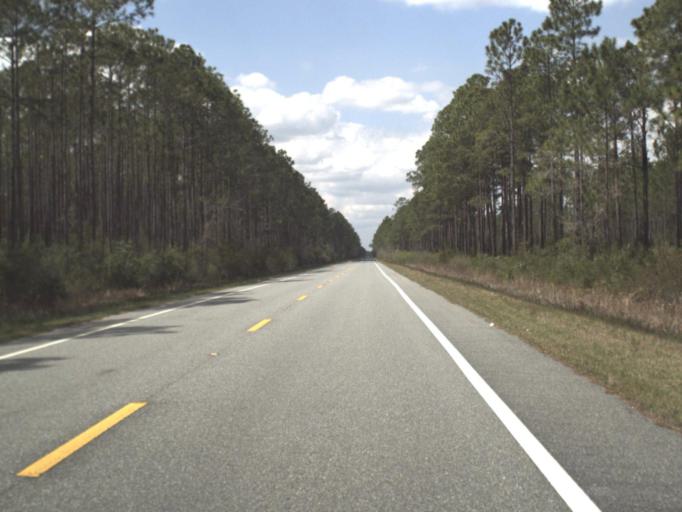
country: US
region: Florida
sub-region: Franklin County
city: Eastpoint
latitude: 29.8381
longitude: -84.9356
